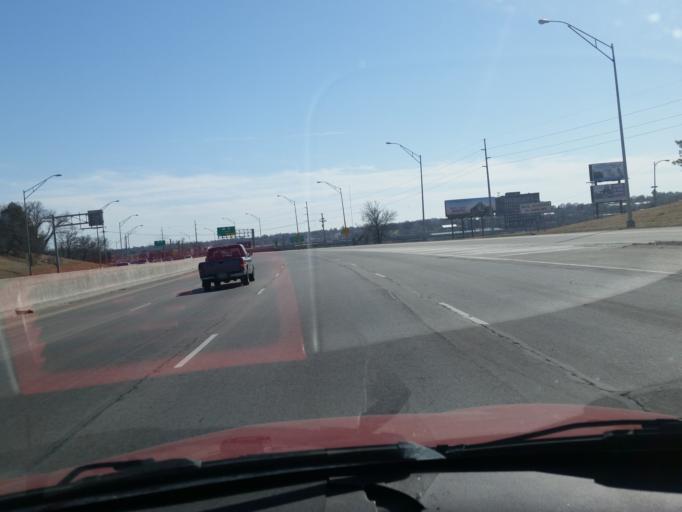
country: US
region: Nebraska
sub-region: Douglas County
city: Omaha
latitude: 41.2179
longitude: -95.9538
